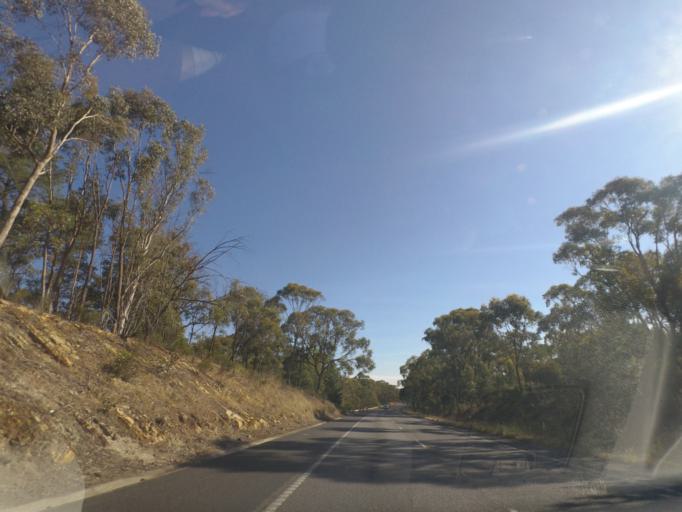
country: AU
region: Victoria
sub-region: Murrindindi
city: Kinglake West
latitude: -37.1719
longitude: 145.0756
